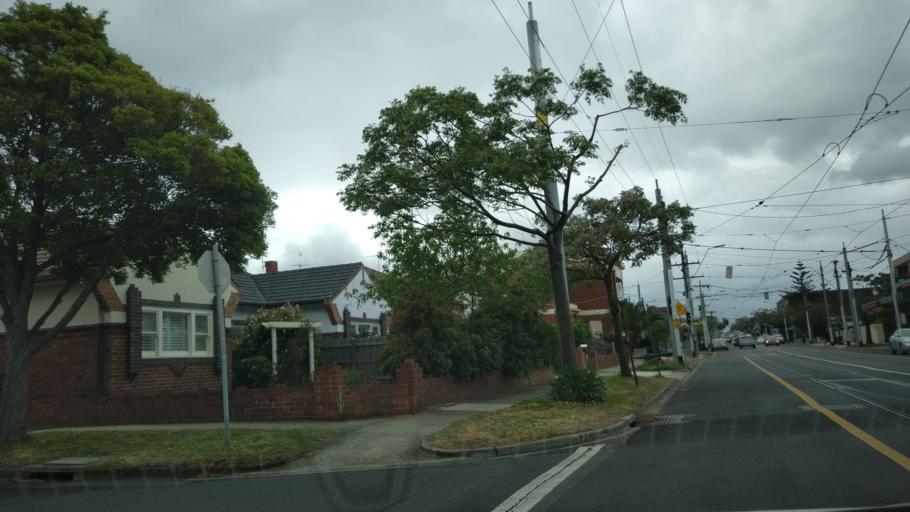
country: AU
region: Victoria
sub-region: Glen Eira
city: Caulfield
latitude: -37.8874
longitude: 145.0261
